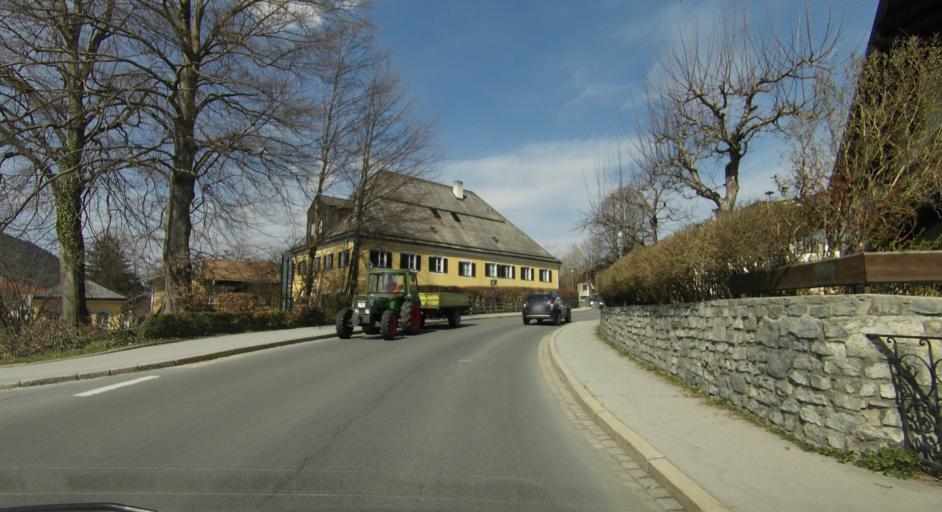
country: DE
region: Bavaria
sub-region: Upper Bavaria
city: Schliersee
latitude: 47.7337
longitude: 11.8650
